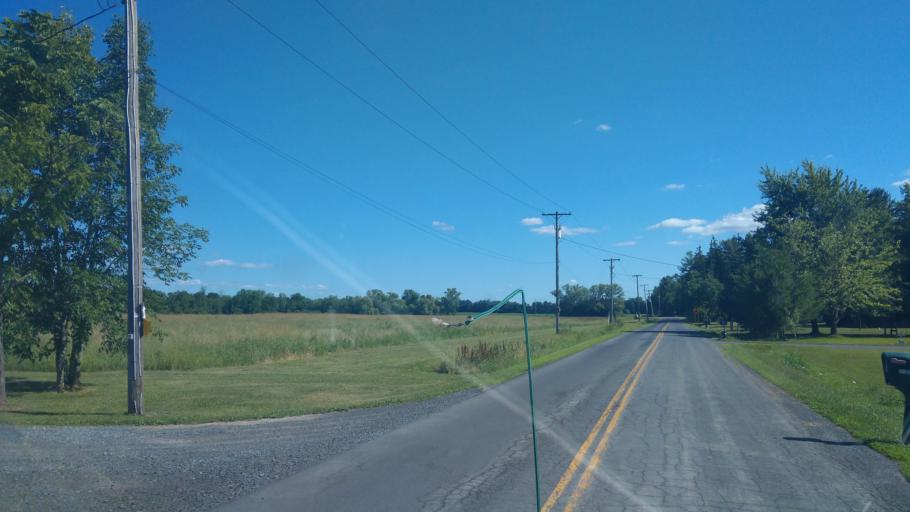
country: US
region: New York
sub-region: Seneca County
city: Seneca Falls
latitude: 42.9585
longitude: -76.8160
